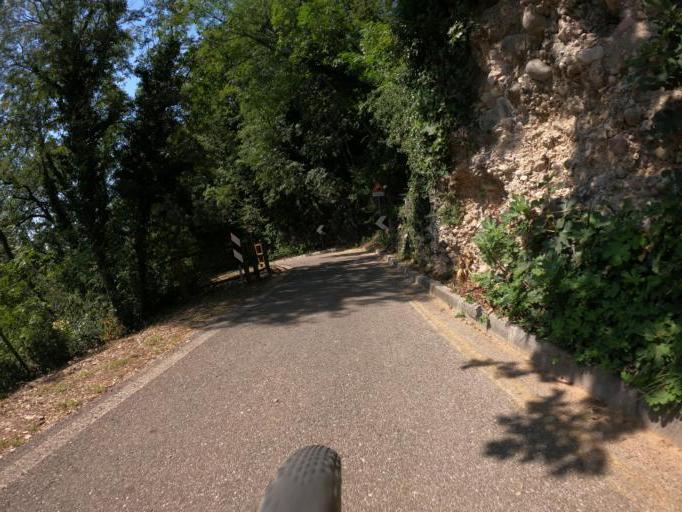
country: IT
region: Veneto
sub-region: Provincia di Verona
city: Volargne
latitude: 45.5559
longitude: 10.8236
